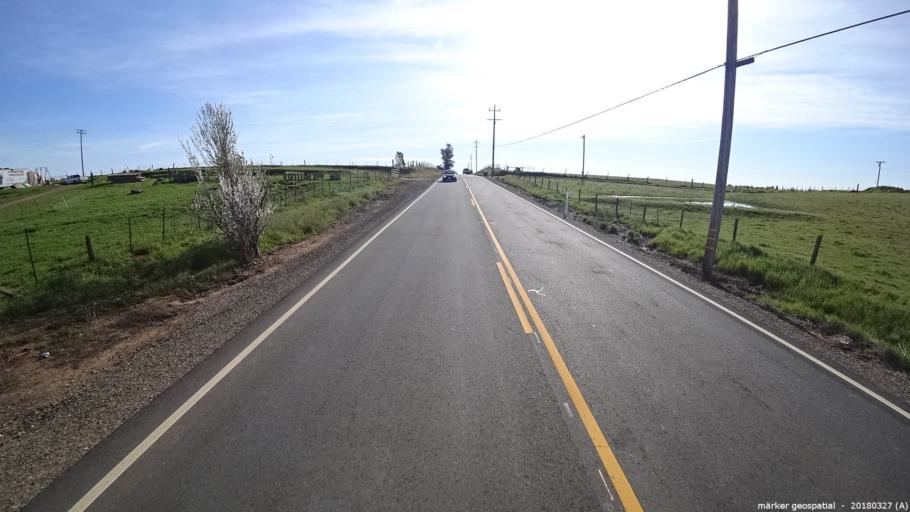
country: US
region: California
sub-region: Sacramento County
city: Vineyard
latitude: 38.4964
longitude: -121.3080
